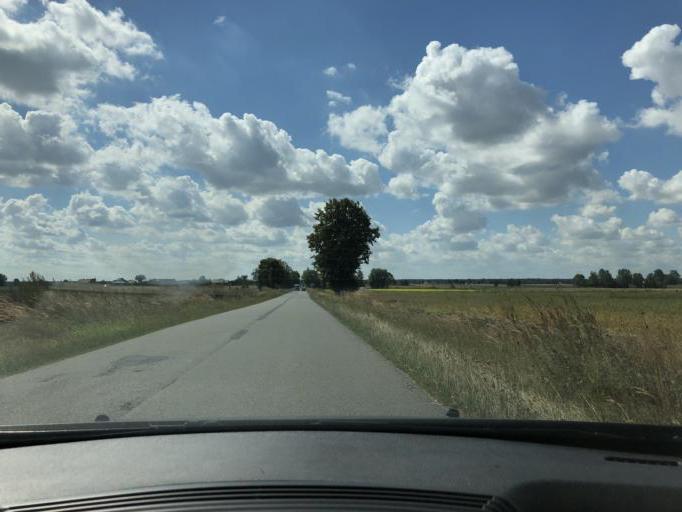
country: PL
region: Lodz Voivodeship
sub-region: Powiat wieruszowski
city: Walichnowy
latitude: 51.2531
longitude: 18.3901
